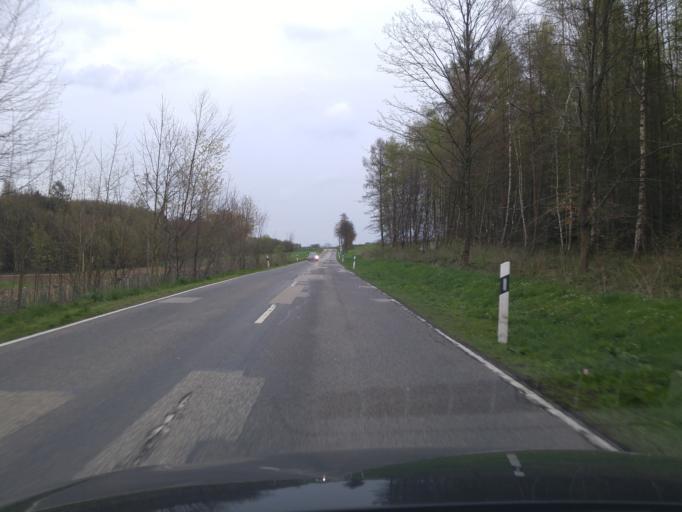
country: DE
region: Baden-Wuerttemberg
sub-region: Karlsruhe Region
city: Reichartshausen
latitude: 49.3667
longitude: 8.9230
